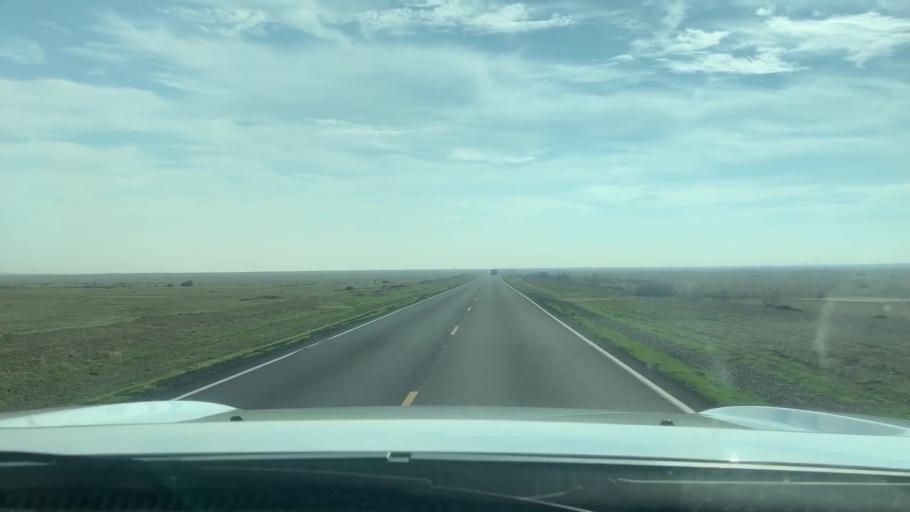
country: US
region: California
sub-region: Kern County
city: Lost Hills
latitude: 35.5786
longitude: -119.8230
